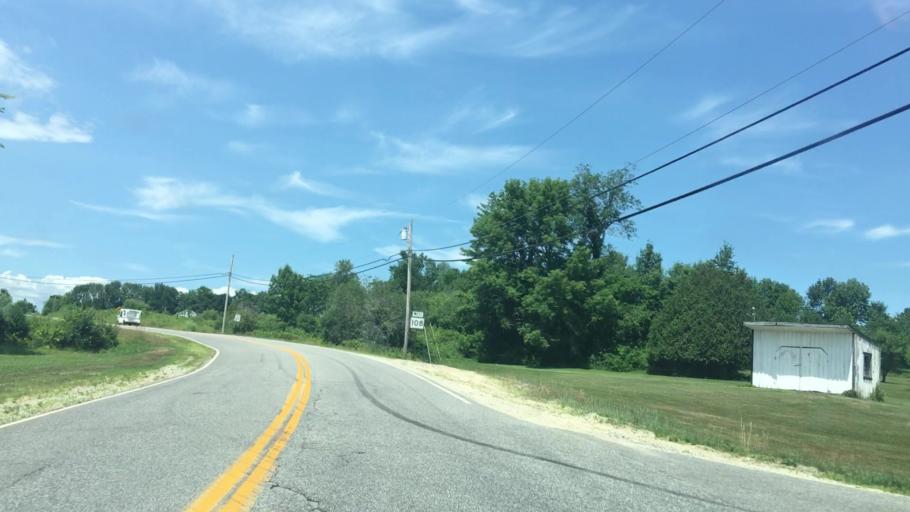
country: US
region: Maine
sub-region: Androscoggin County
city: Livermore
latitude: 44.3837
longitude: -70.2078
